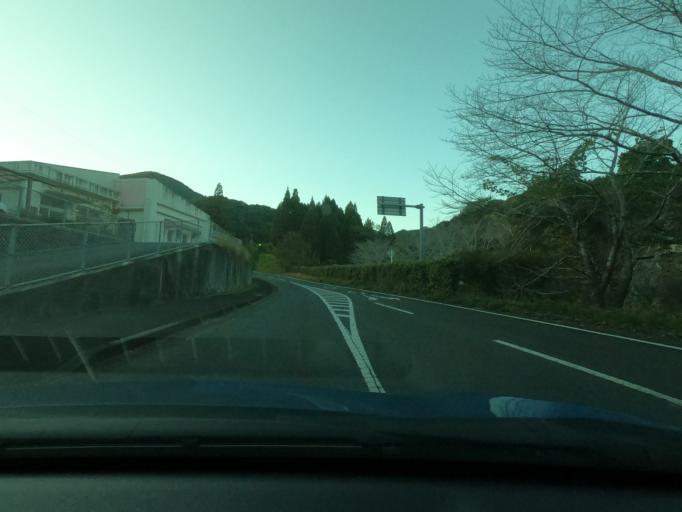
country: JP
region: Kagoshima
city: Satsumasendai
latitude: 31.8098
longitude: 130.4858
